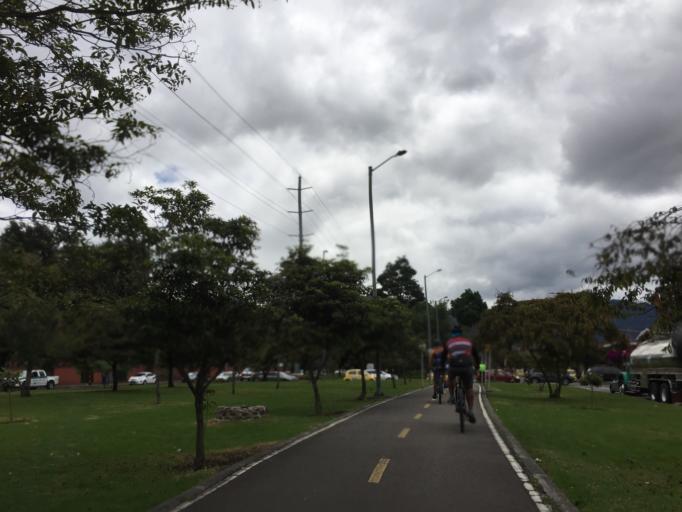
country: CO
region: Bogota D.C.
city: Bogota
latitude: 4.6510
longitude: -74.0921
